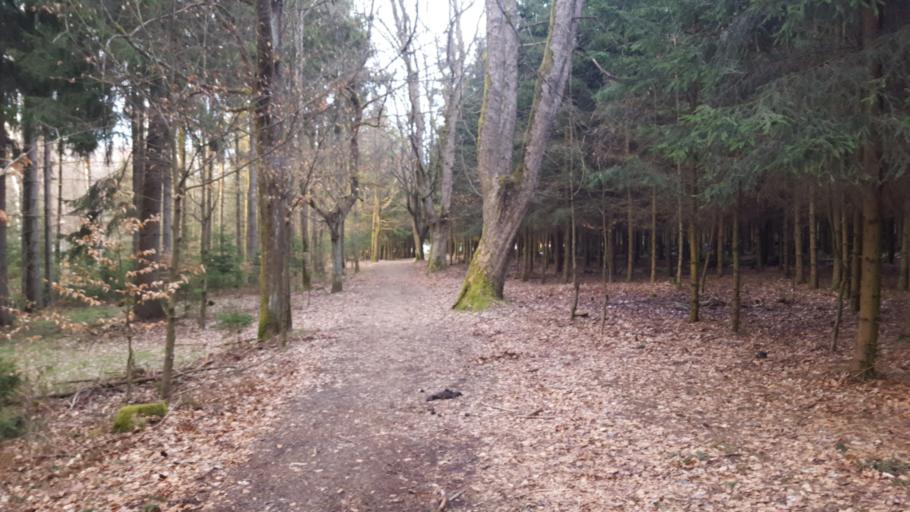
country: CZ
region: Karlovarsky
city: As
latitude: 50.2291
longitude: 12.2014
